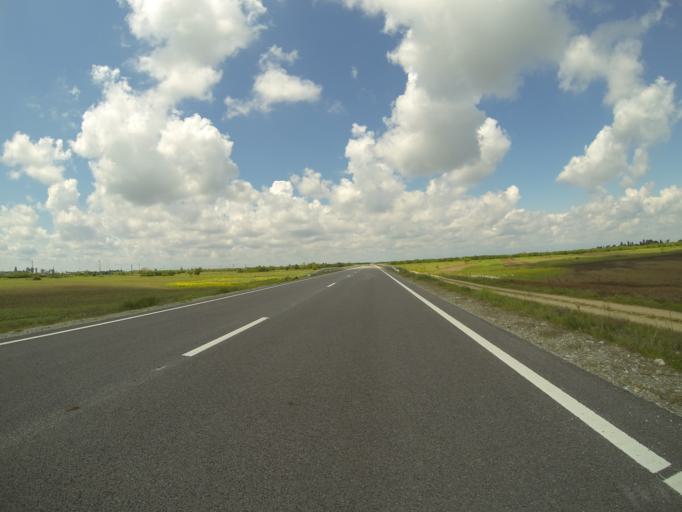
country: RO
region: Dolj
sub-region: Comuna Carcea
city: Carcea
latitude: 44.2751
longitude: 23.9102
